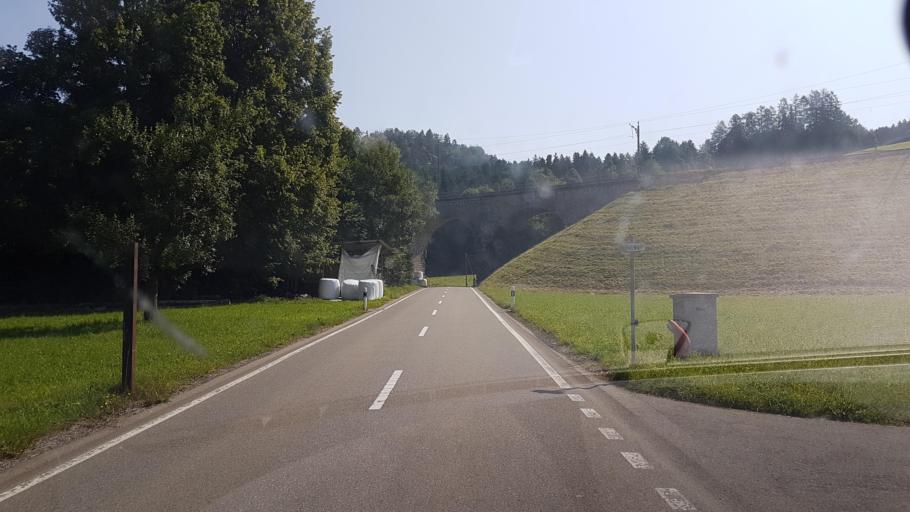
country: CH
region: Saint Gallen
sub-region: Wahlkreis Toggenburg
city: Mogelsberg
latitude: 47.3550
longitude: 9.1342
